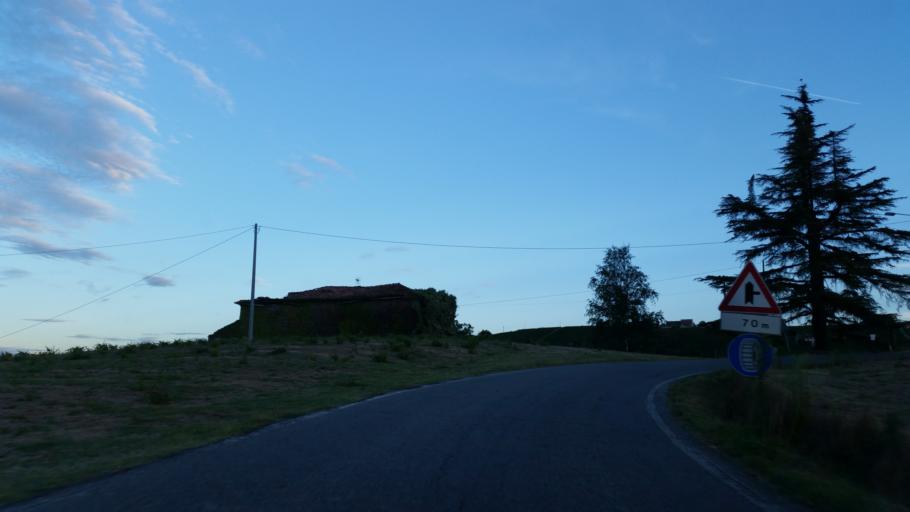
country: IT
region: Piedmont
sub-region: Provincia di Cuneo
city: Castiglione Tinella
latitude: 44.7268
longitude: 8.1933
